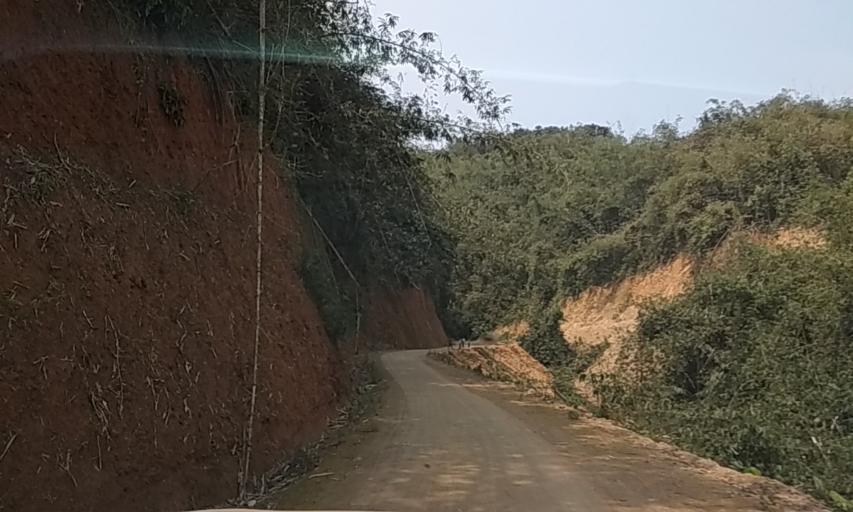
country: LA
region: Phongsali
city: Phongsali
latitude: 21.4702
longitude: 102.4302
